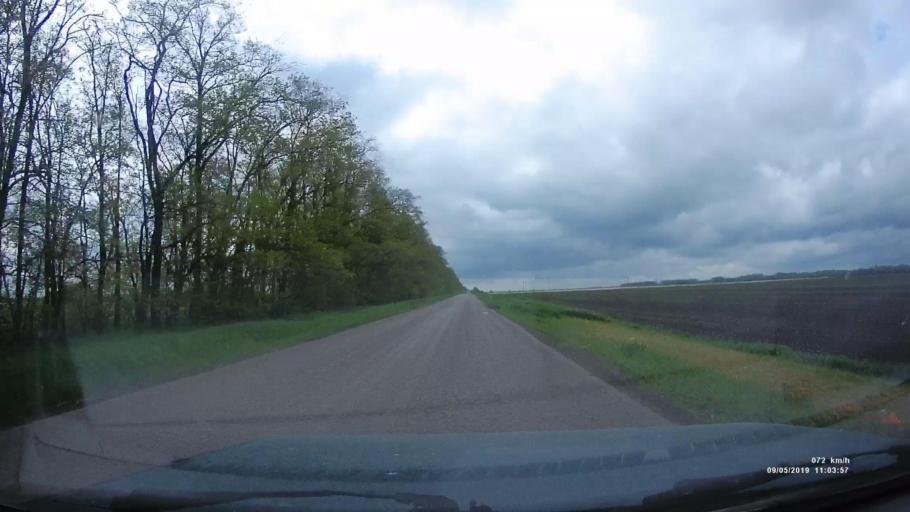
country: RU
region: Krasnodarskiy
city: Kanelovskaya
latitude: 46.8228
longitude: 39.2100
